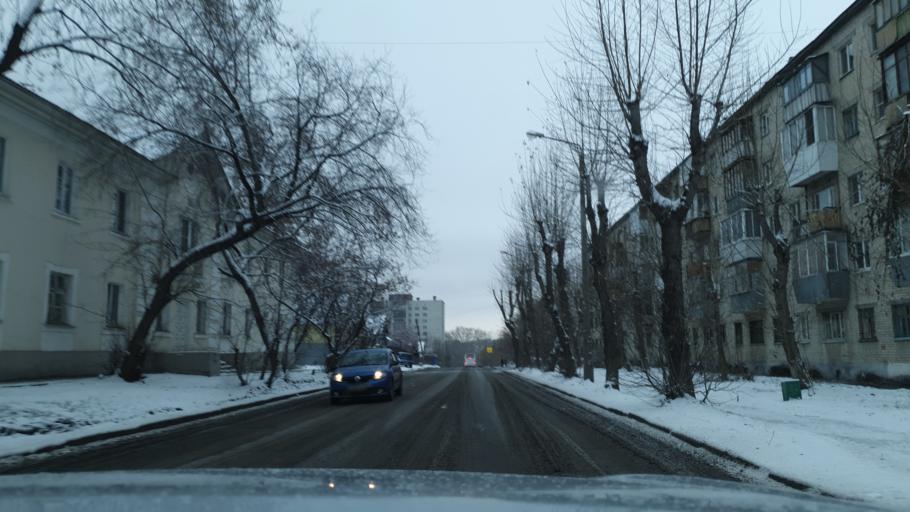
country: RU
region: Sverdlovsk
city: Istok
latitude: 56.7496
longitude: 60.7090
